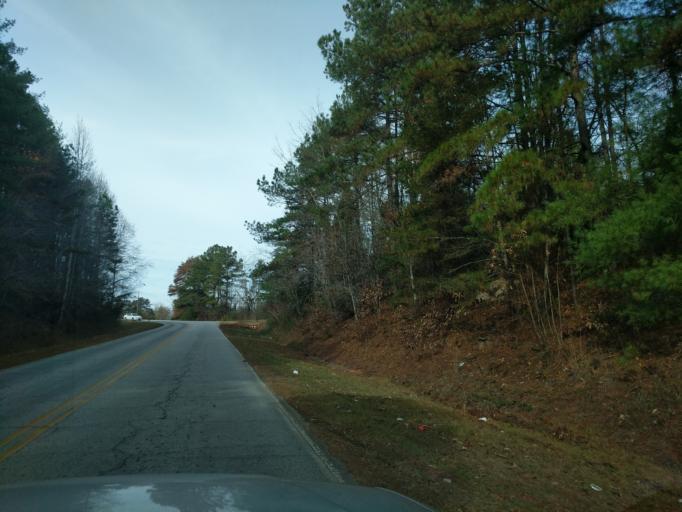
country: US
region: South Carolina
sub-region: Oconee County
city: Walhalla
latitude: 34.8028
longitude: -83.0298
